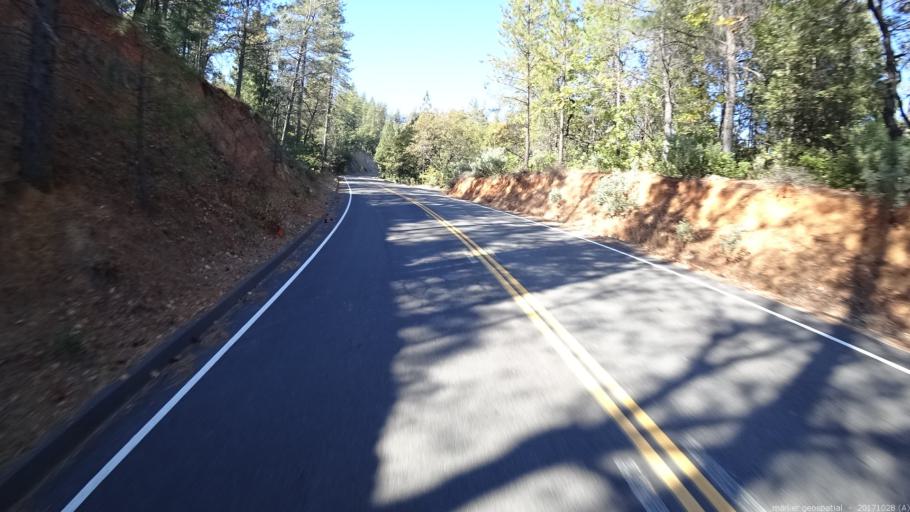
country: US
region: California
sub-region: Shasta County
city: Shasta
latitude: 40.6064
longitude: -122.5573
